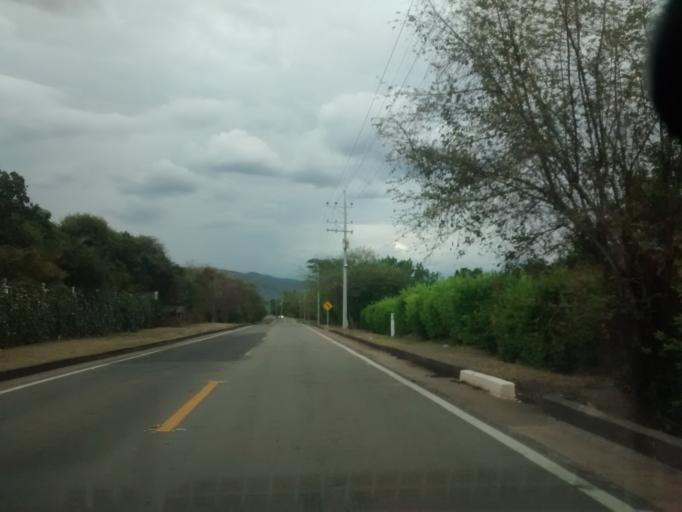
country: CO
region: Cundinamarca
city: Tocaima
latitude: 4.4464
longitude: -74.6619
